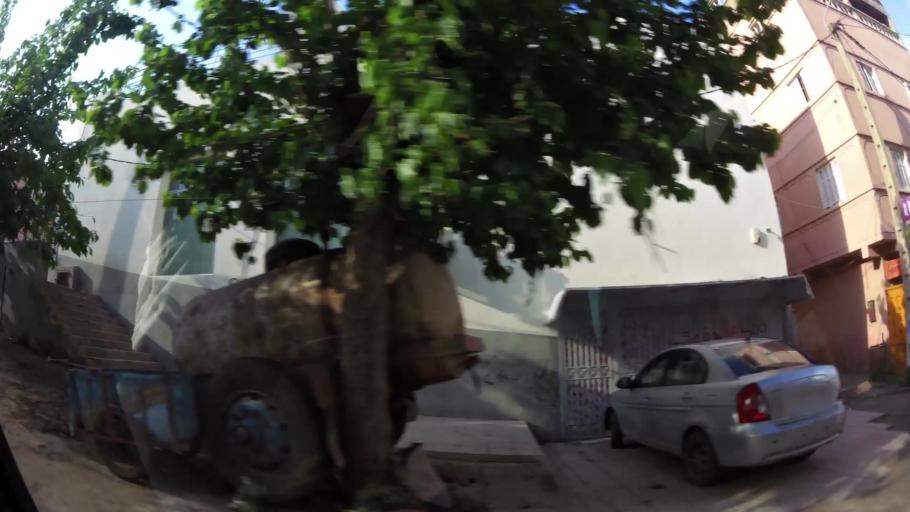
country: MA
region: Chaouia-Ouardigha
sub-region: Settat Province
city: Settat
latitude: 33.0047
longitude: -7.6277
